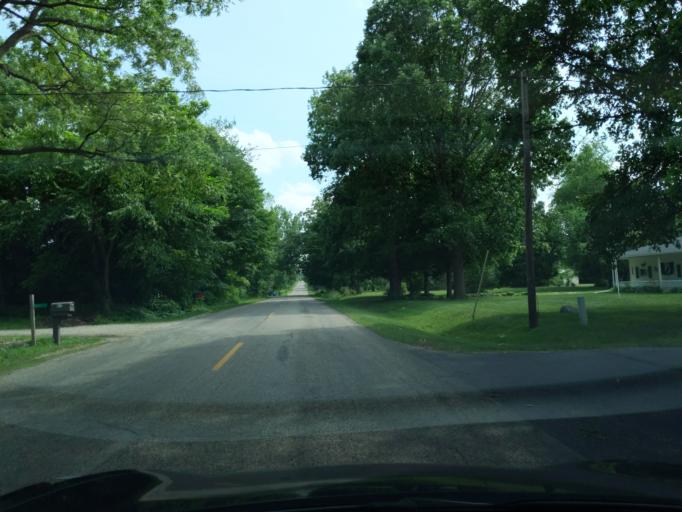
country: US
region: Michigan
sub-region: Eaton County
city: Eaton Rapids
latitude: 42.5645
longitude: -84.6021
